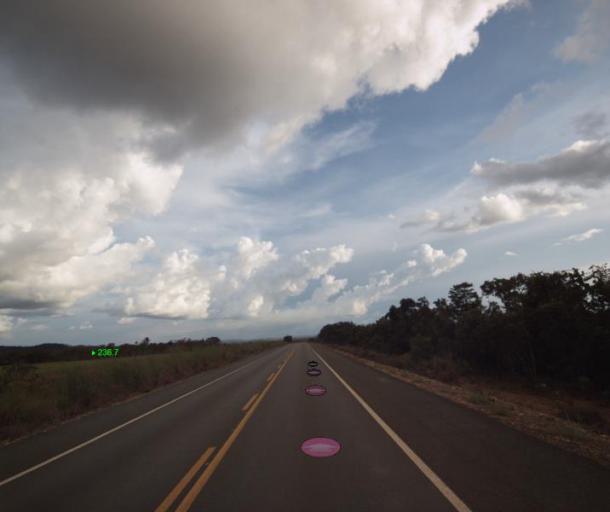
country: BR
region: Goias
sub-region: Niquelandia
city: Niquelandia
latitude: -14.7124
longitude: -48.6058
